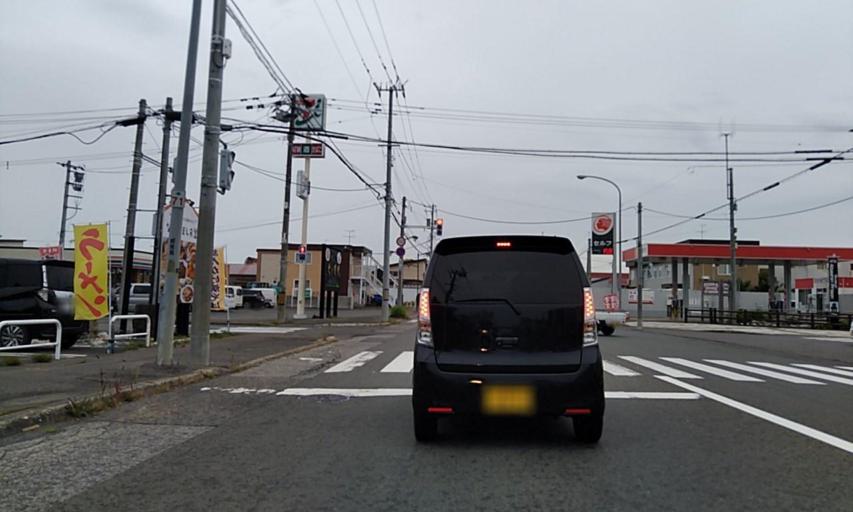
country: JP
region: Hokkaido
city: Bihoro
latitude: 43.9142
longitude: 144.1744
